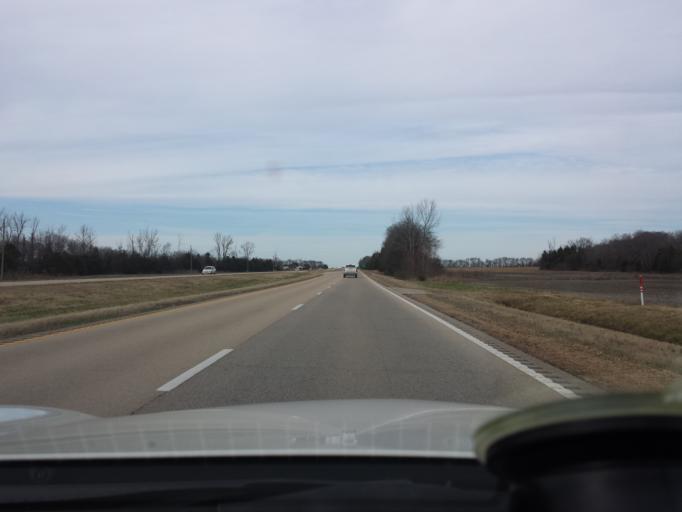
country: US
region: Mississippi
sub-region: Monroe County
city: Aberdeen
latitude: 33.8156
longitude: -88.7032
